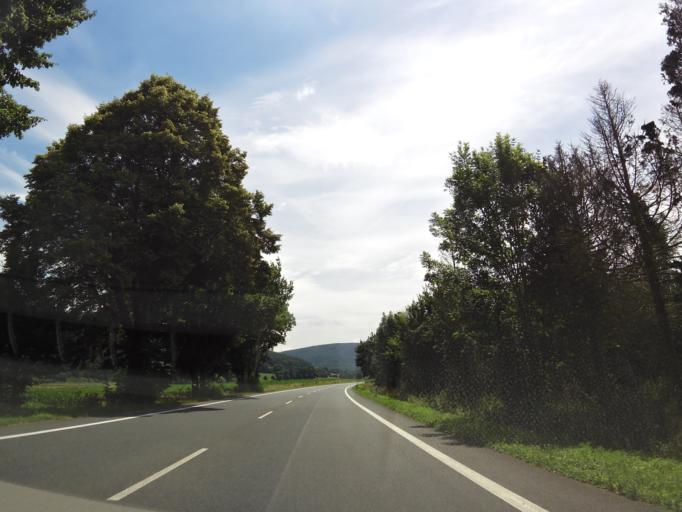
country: DE
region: Lower Saxony
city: Bodenfelde
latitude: 51.5599
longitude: 9.6030
